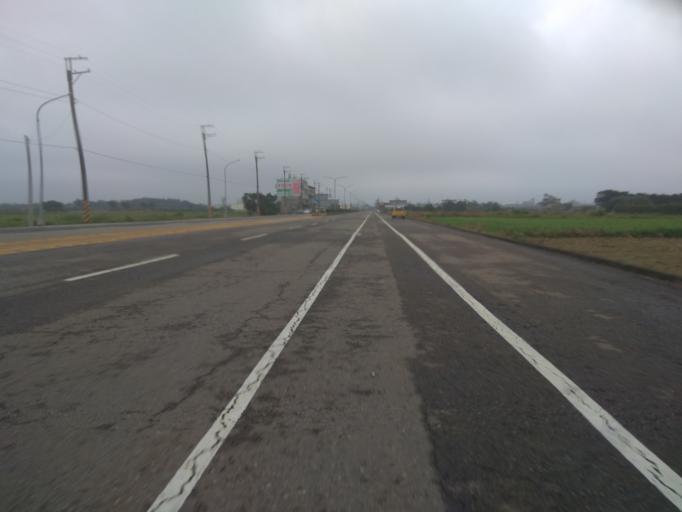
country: TW
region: Taiwan
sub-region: Hsinchu
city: Zhubei
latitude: 25.0249
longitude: 121.0812
